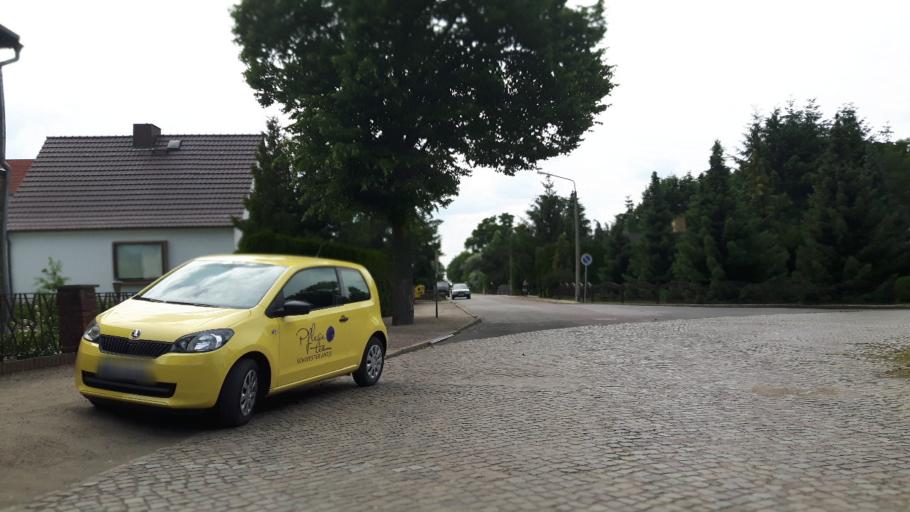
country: DE
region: Saxony-Anhalt
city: Bergwitz
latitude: 51.8035
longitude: 12.5729
